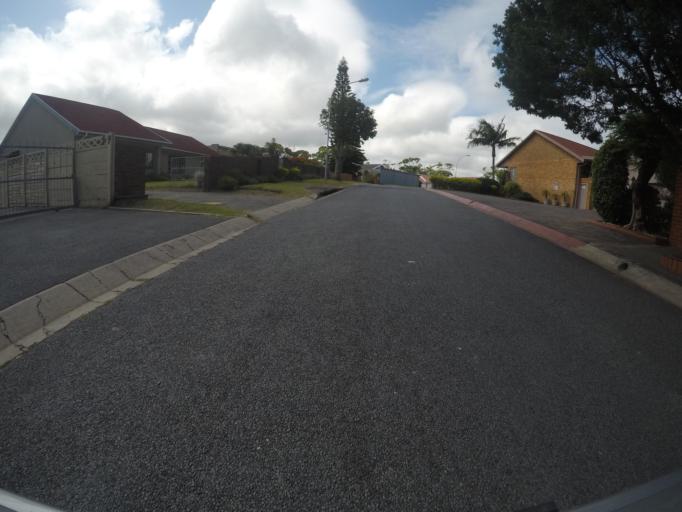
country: ZA
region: Eastern Cape
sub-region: Buffalo City Metropolitan Municipality
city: East London
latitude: -32.9979
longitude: 27.8861
